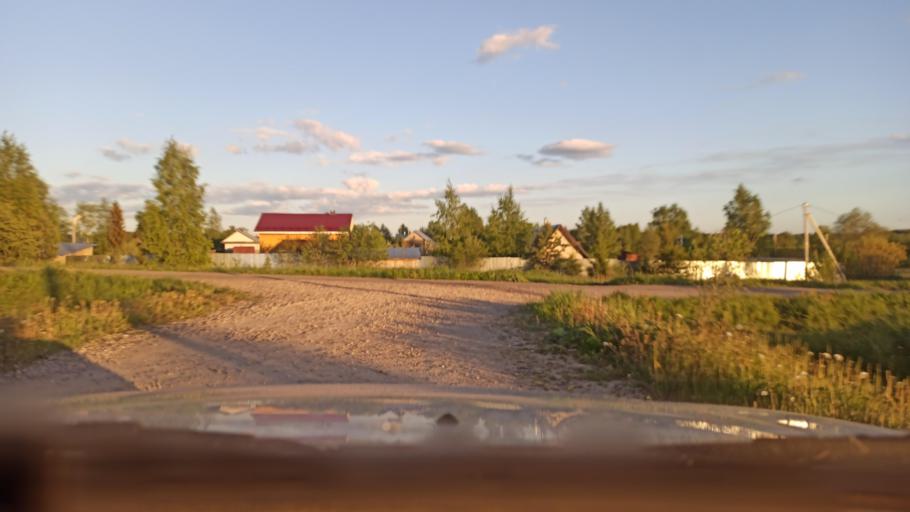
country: RU
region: Vologda
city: Molochnoye
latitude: 59.3717
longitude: 39.6952
